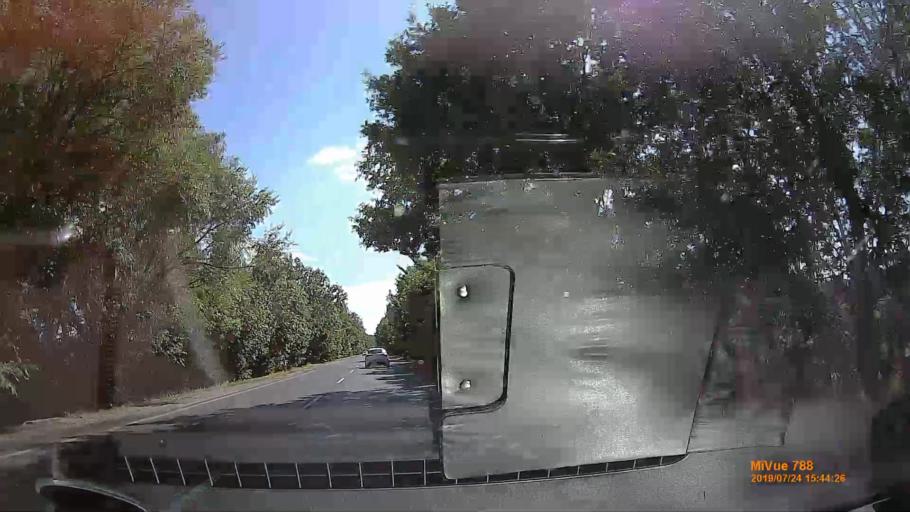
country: HU
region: Szabolcs-Szatmar-Bereg
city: Vasarosnameny
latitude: 48.0999
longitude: 22.2943
